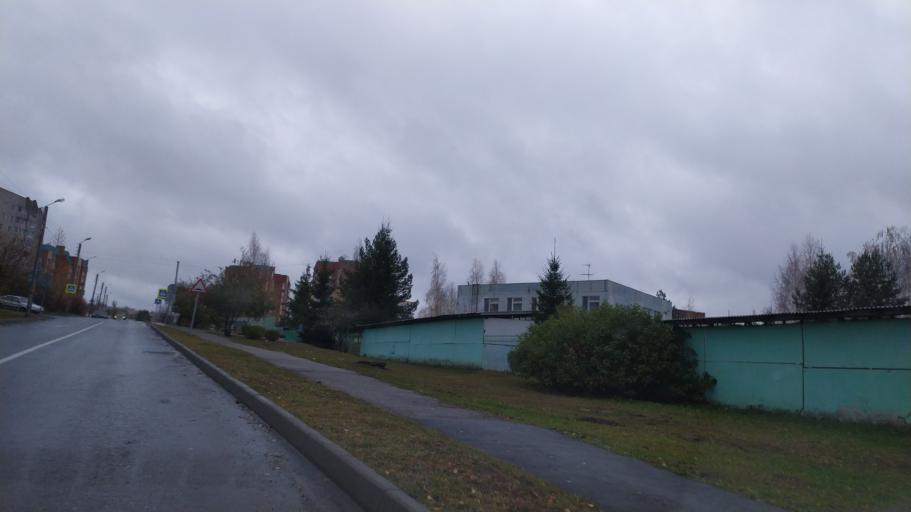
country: RU
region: Chuvashia
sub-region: Cheboksarskiy Rayon
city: Cheboksary
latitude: 56.1458
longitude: 47.1618
